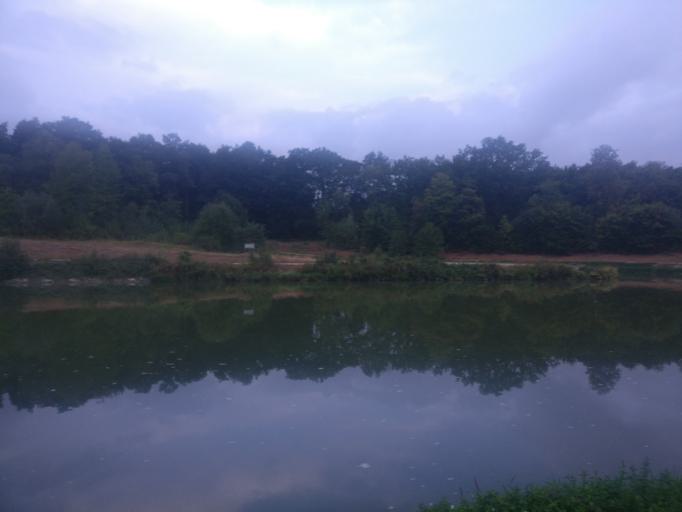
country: DE
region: Bavaria
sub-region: Regierungsbezirk Mittelfranken
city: Mohrendorf
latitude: 49.6312
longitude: 10.9867
